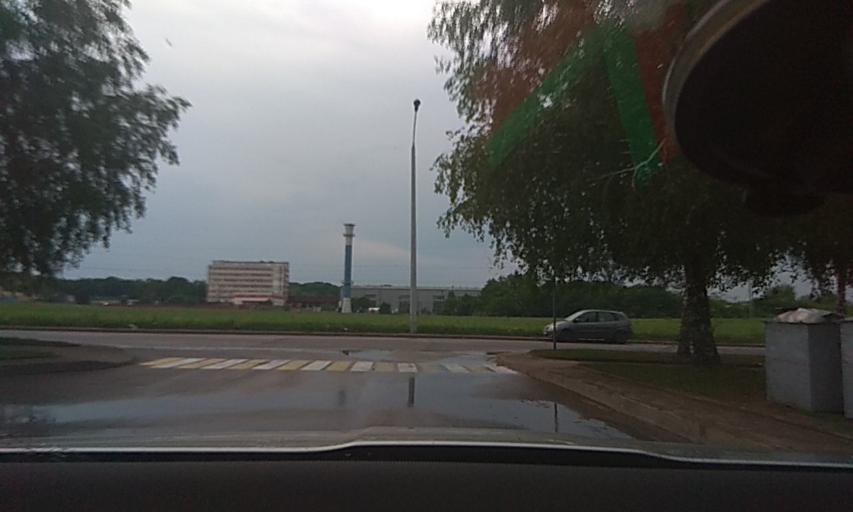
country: BY
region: Grodnenskaya
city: Hrodna
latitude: 53.6787
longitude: 23.8944
